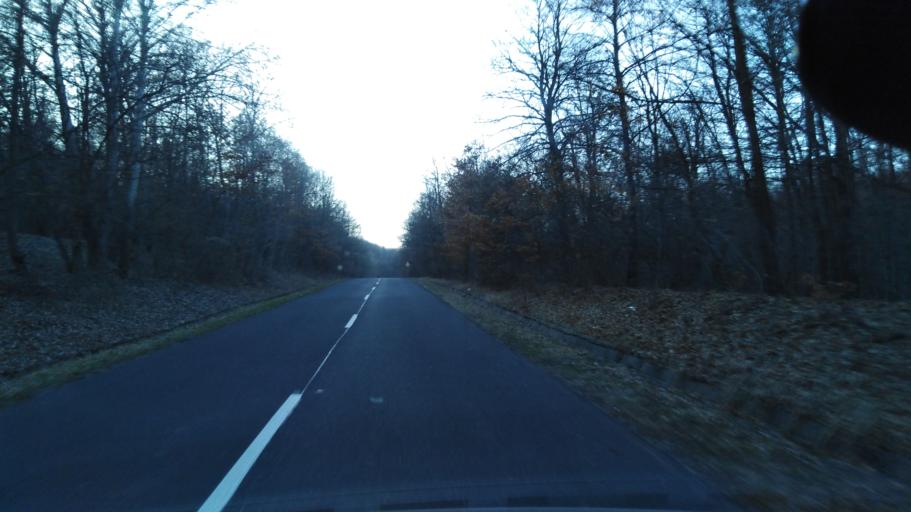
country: HU
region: Nograd
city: Salgotarjan
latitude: 48.0665
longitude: 19.8234
